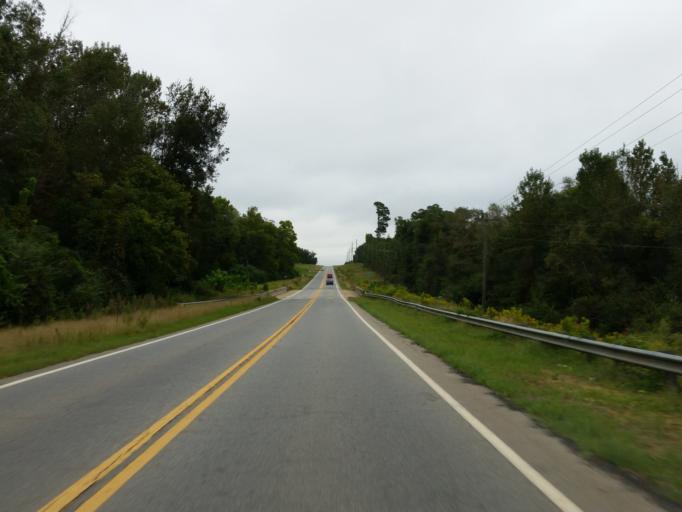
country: US
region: Georgia
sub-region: Houston County
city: Perry
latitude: 32.4860
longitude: -83.7829
